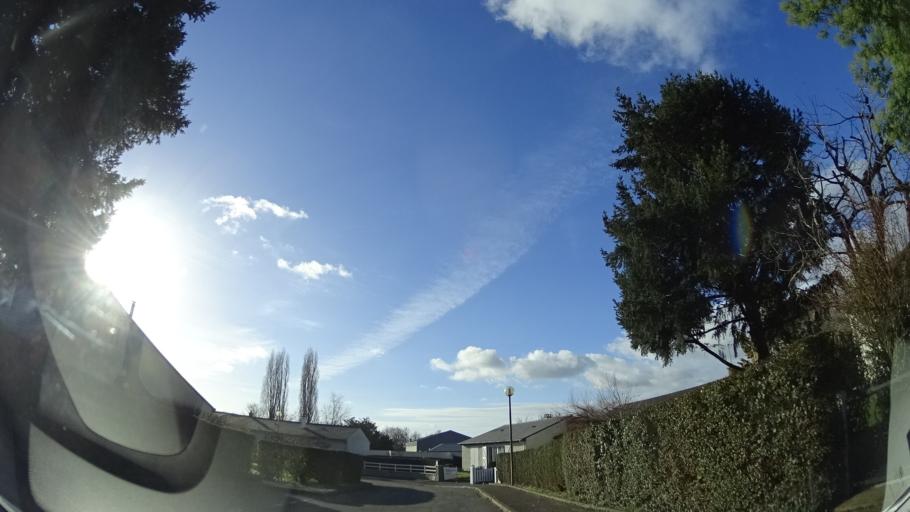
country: FR
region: Brittany
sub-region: Departement d'Ille-et-Vilaine
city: Betton
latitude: 48.1781
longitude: -1.6357
